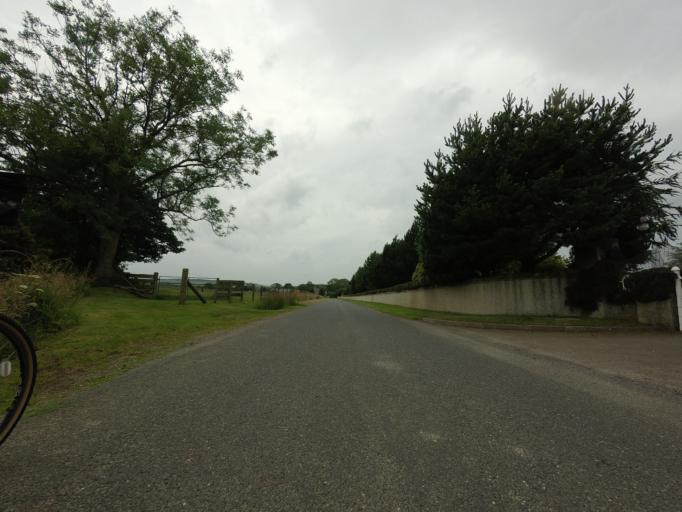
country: GB
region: Scotland
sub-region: Aberdeenshire
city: Portsoy
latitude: 57.6620
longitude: -2.7403
